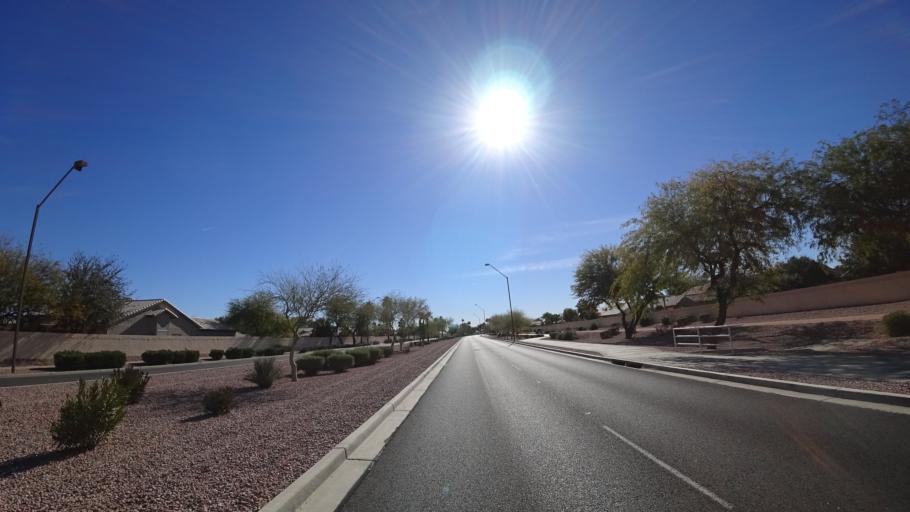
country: US
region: Arizona
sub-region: Maricopa County
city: Litchfield Park
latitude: 33.4853
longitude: -112.3957
